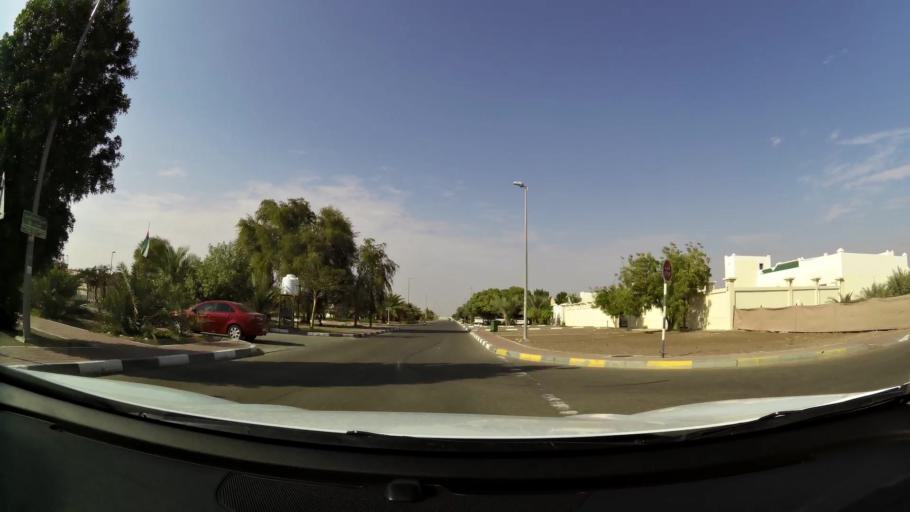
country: AE
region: Abu Dhabi
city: Al Ain
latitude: 24.0834
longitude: 55.8684
